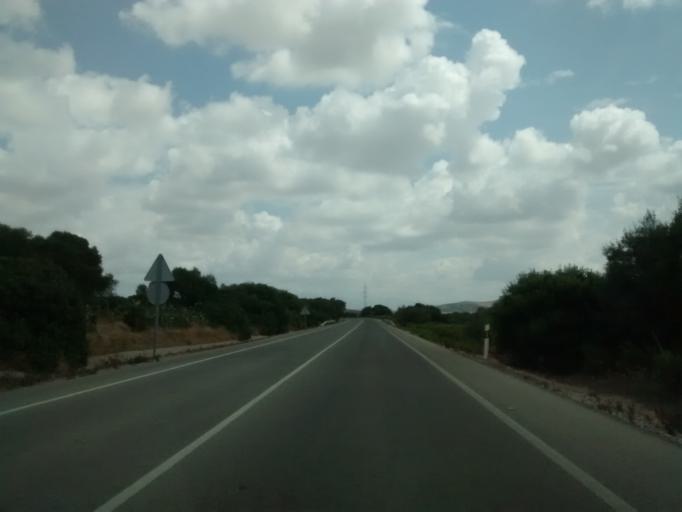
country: ES
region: Andalusia
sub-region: Provincia de Cadiz
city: Medina Sidonia
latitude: 36.4442
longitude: -5.8973
